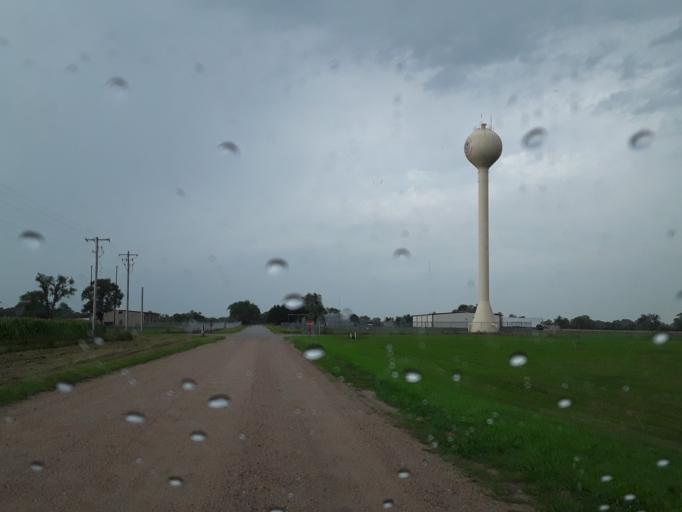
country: US
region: Nebraska
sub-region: Saunders County
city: Yutan
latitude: 41.1844
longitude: -96.4449
